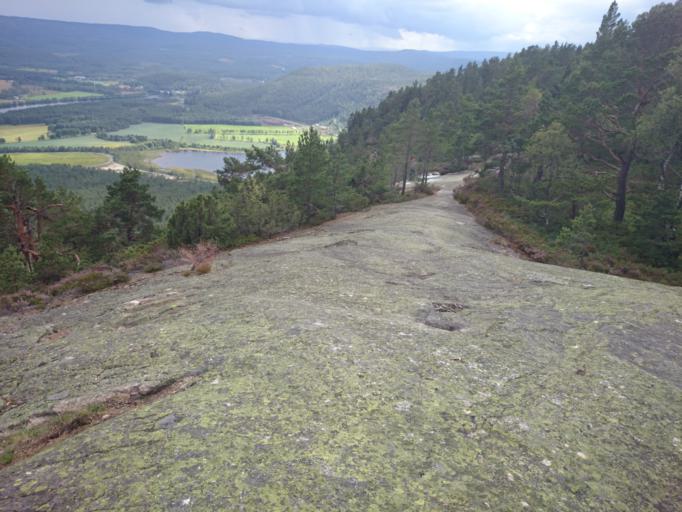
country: NO
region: Aust-Agder
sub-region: Amli
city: Amli
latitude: 58.7705
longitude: 8.4659
